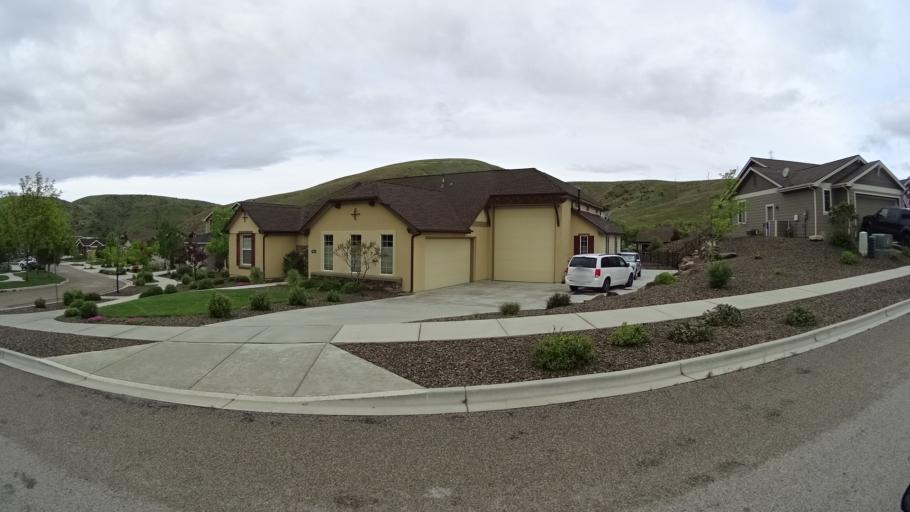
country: US
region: Idaho
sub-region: Ada County
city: Eagle
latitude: 43.7679
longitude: -116.2636
